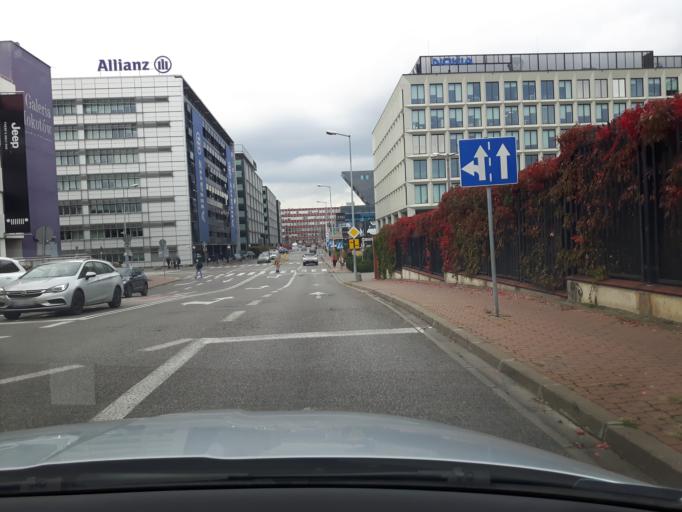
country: PL
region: Masovian Voivodeship
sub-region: Warszawa
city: Mokotow
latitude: 52.1805
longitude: 21.0061
